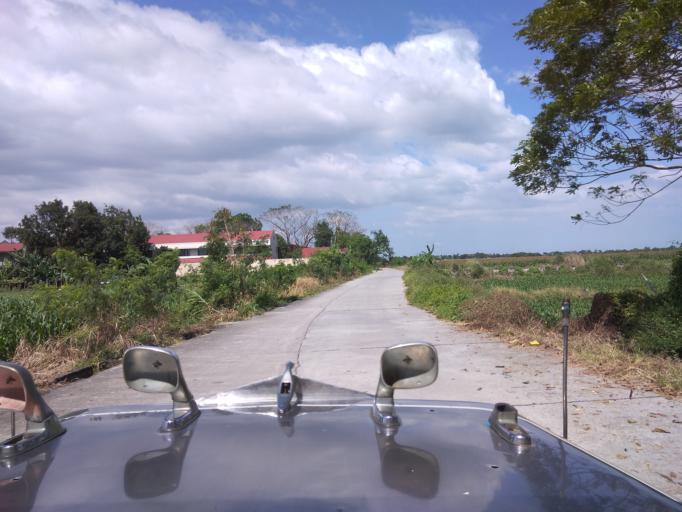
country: PH
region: Central Luzon
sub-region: Province of Pampanga
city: Anao
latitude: 15.1280
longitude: 120.7007
